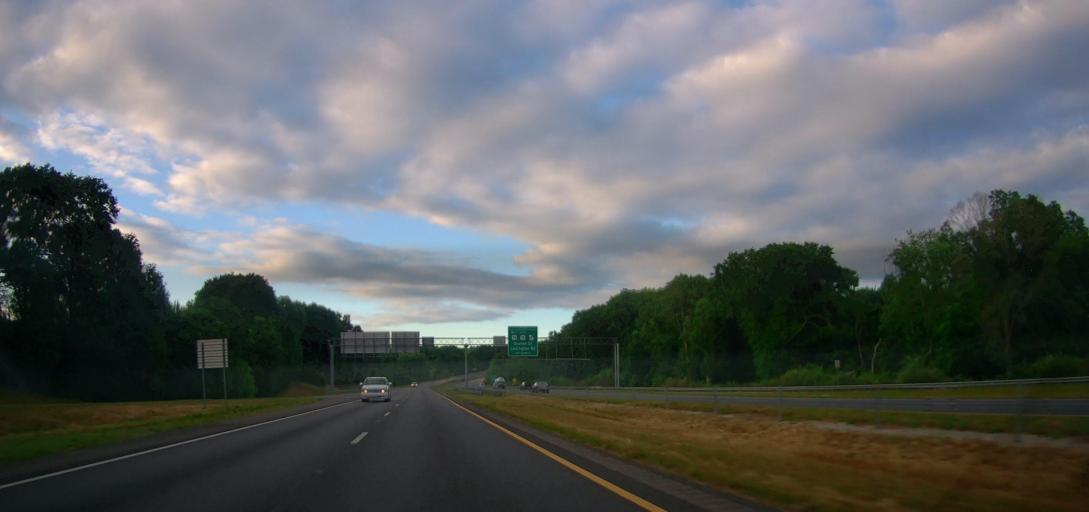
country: US
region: Georgia
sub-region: Clarke County
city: Athens
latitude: 33.9365
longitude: -83.3662
